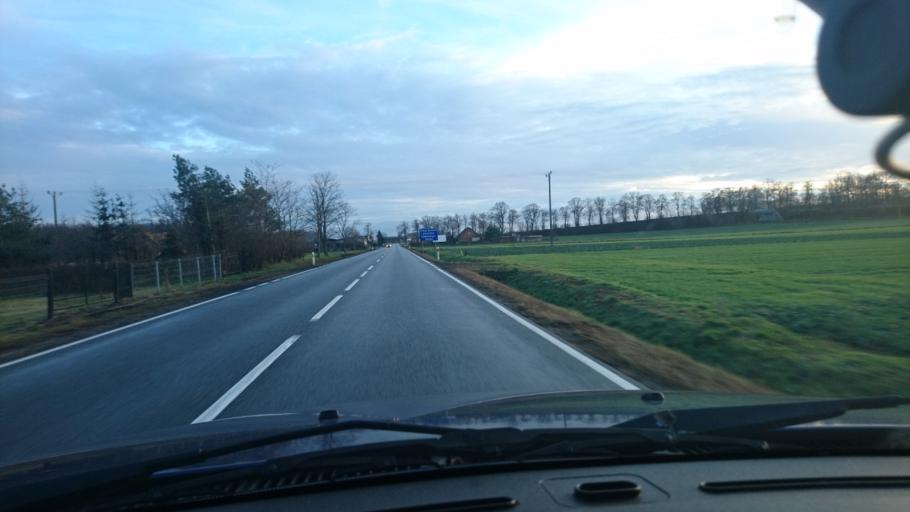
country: PL
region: Opole Voivodeship
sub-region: Powiat kluczborski
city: Byczyna
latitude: 51.1395
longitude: 18.1962
